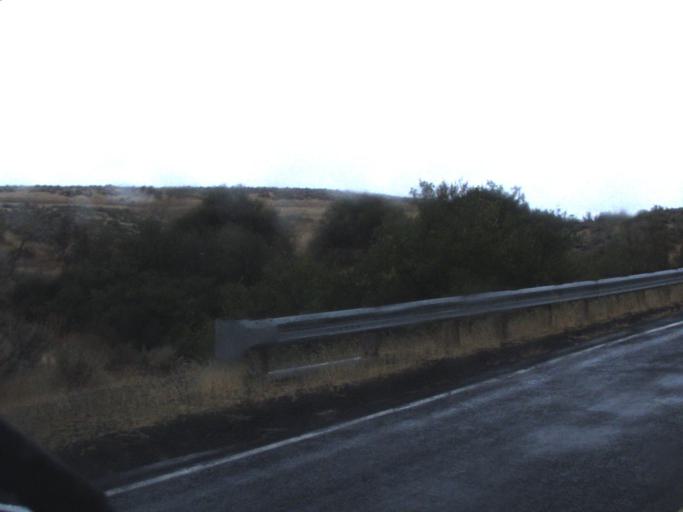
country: US
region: Washington
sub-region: Lincoln County
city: Davenport
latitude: 47.3534
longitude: -118.1022
